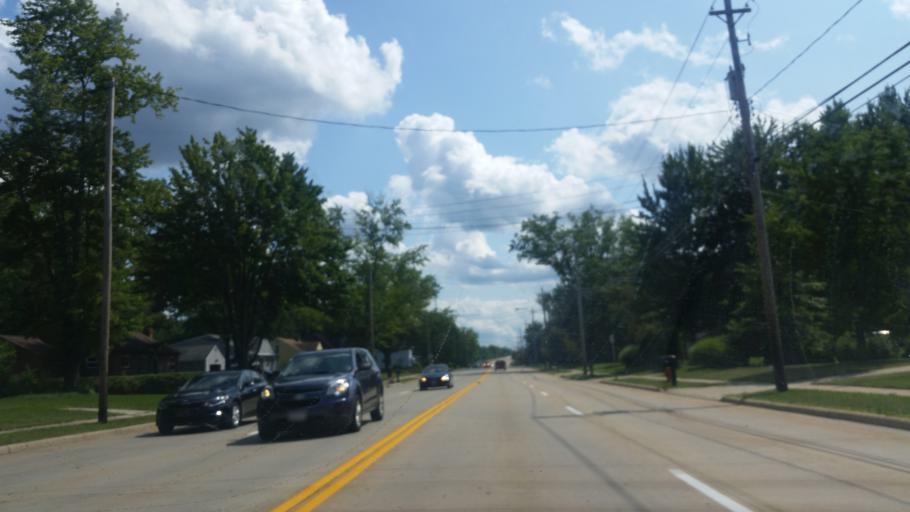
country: US
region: Ohio
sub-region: Cuyahoga County
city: North Olmsted
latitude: 41.4035
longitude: -81.9435
